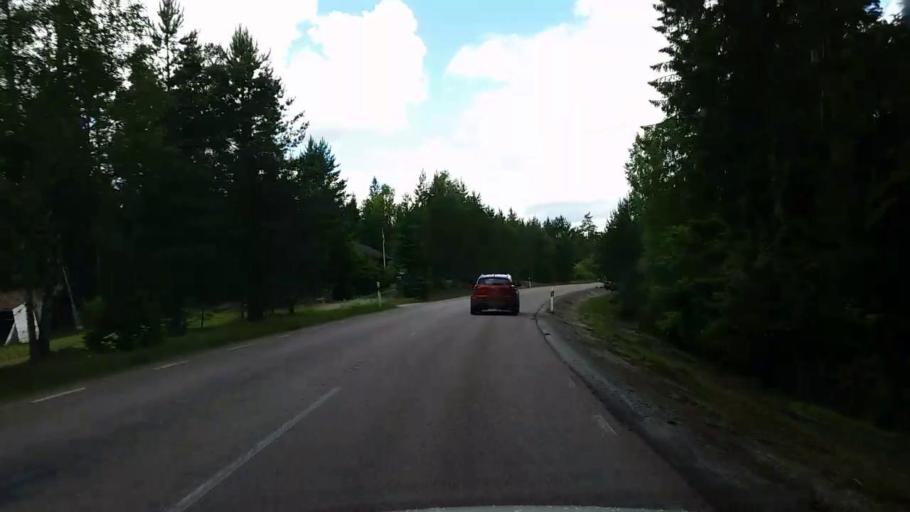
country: SE
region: Vaestmanland
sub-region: Fagersta Kommun
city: Fagersta
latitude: 59.8790
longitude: 15.8367
